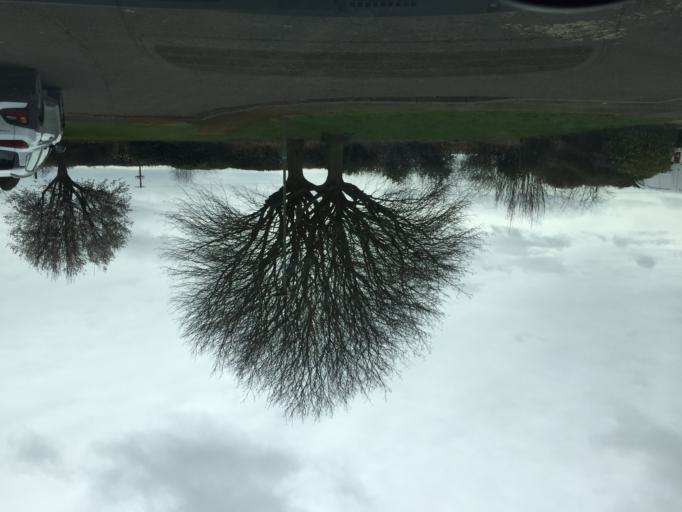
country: GB
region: England
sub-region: Oxfordshire
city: Banbury
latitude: 52.0442
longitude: -1.3370
